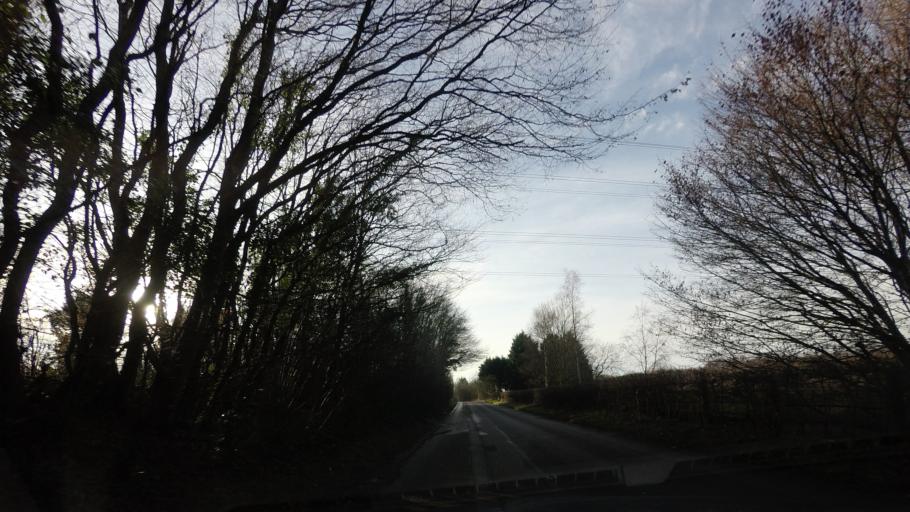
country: GB
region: England
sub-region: East Sussex
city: Bexhill-on-Sea
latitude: 50.8894
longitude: 0.4371
